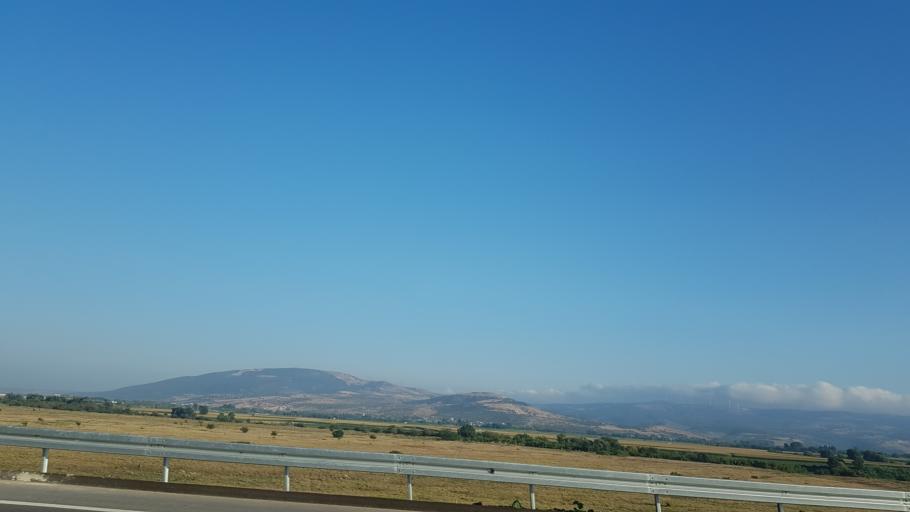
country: TR
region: Bursa
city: Karacabey
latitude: 40.2255
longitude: 28.4066
